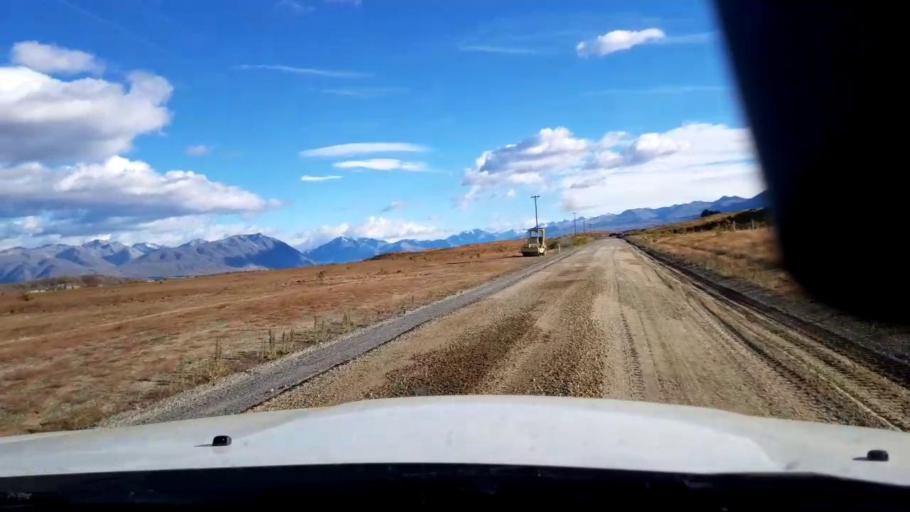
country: NZ
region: Canterbury
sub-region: Timaru District
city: Pleasant Point
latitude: -43.9826
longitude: 170.5079
